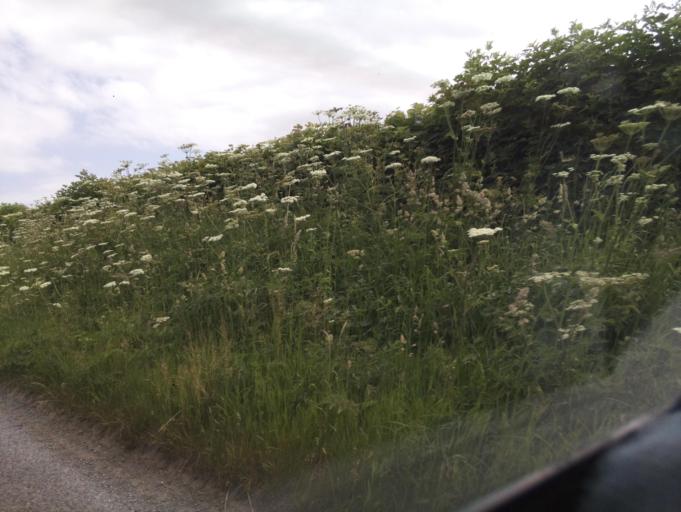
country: GB
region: England
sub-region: Somerset
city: Milborne Port
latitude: 51.0172
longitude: -2.4702
